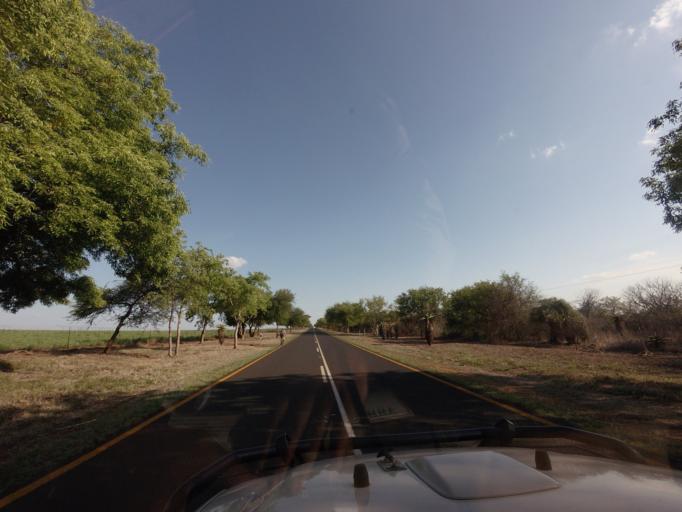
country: ZA
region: Mpumalanga
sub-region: Ehlanzeni District
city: Komatipoort
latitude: -25.3687
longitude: 31.9027
